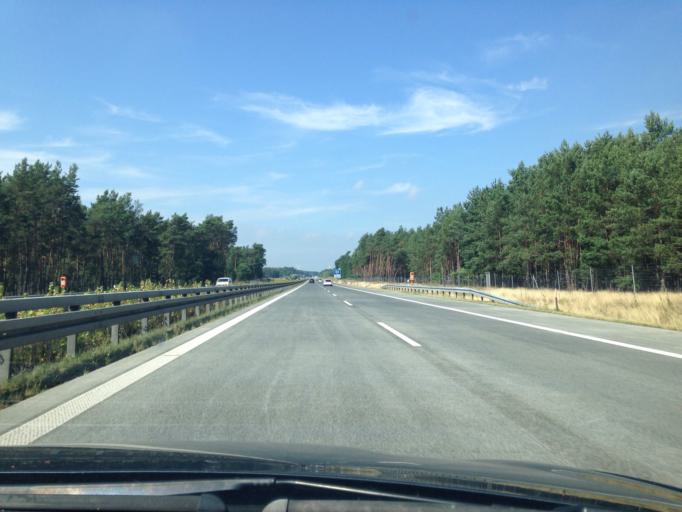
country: DE
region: Brandenburg
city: Luebben
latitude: 51.8840
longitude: 13.8619
